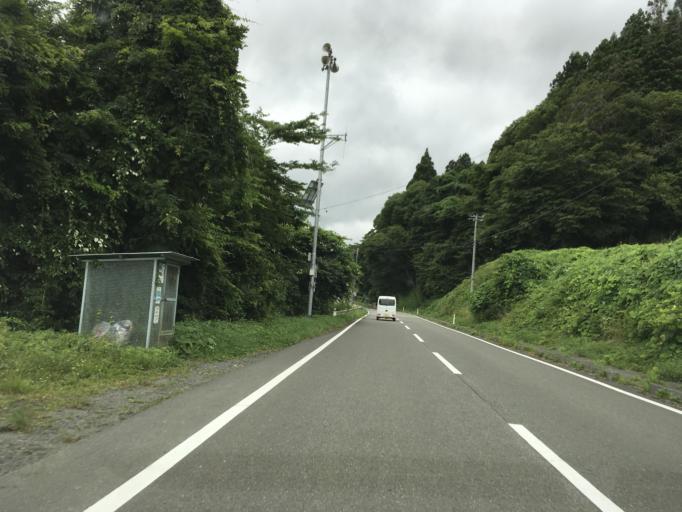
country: JP
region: Iwate
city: Ofunato
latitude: 38.8960
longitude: 141.4867
